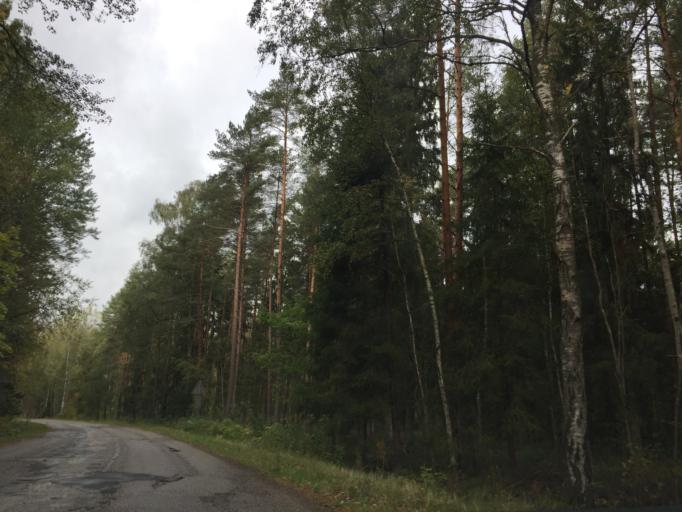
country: LV
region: Olaine
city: Olaine
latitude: 56.7632
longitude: 23.9041
